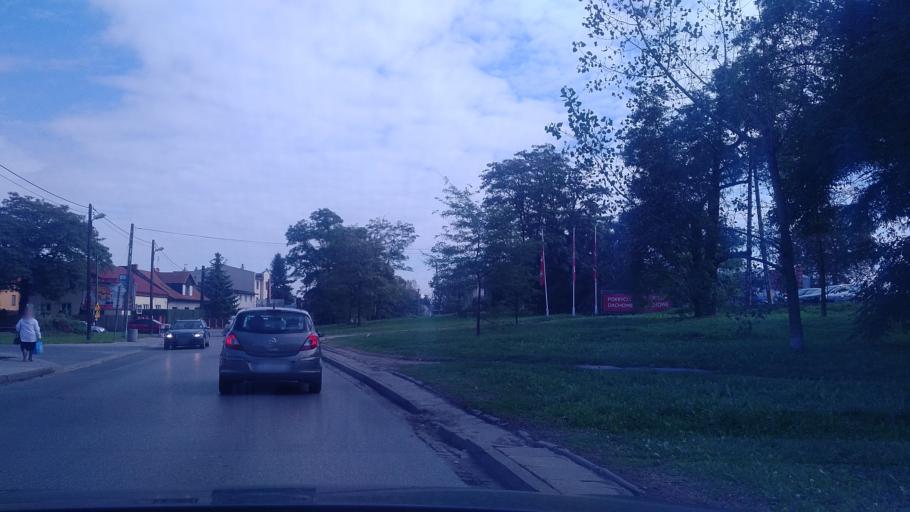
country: PL
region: Lesser Poland Voivodeship
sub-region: Krakow
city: Krakow
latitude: 50.0834
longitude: 19.9072
